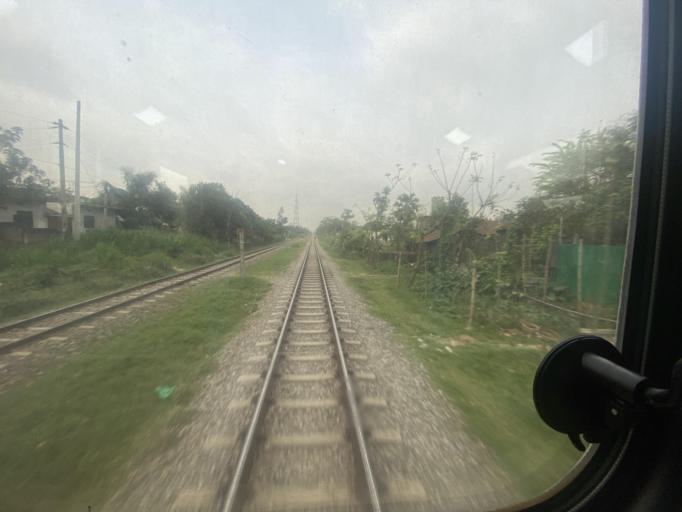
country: BD
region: Dhaka
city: Tungi
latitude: 23.9271
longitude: 90.4524
